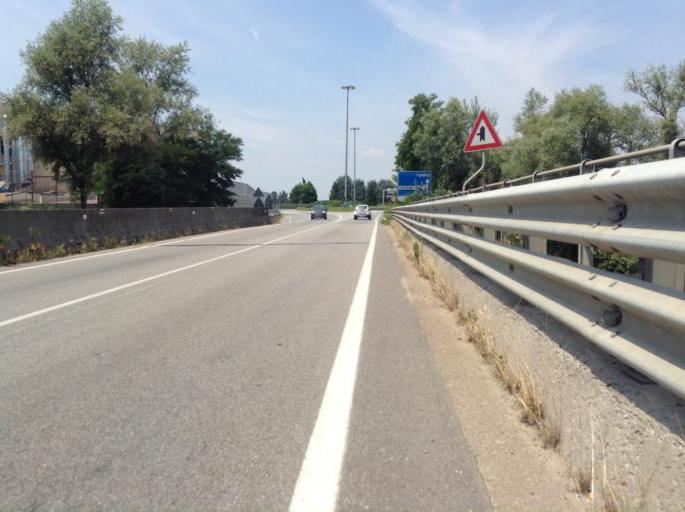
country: IT
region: Piedmont
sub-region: Provincia di Torino
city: Carignano
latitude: 44.9153
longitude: 7.6781
